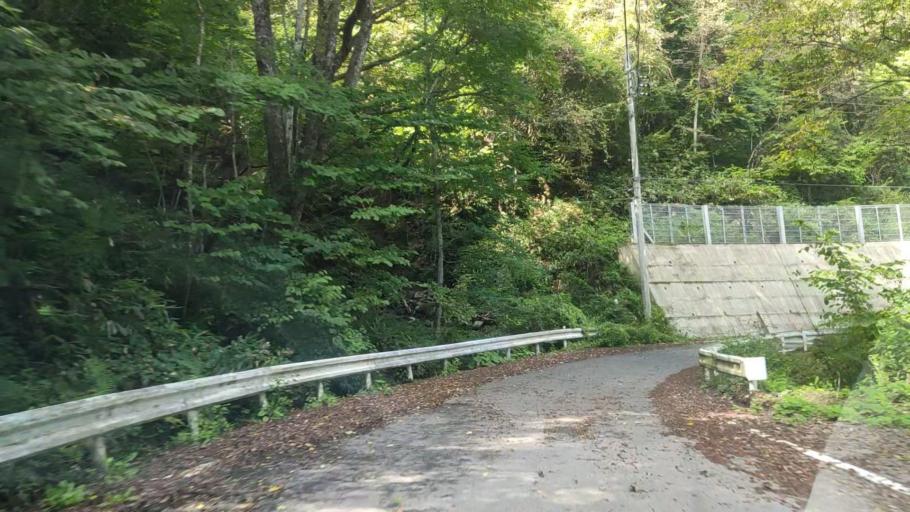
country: JP
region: Gunma
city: Nakanojomachi
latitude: 36.6533
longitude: 138.6191
